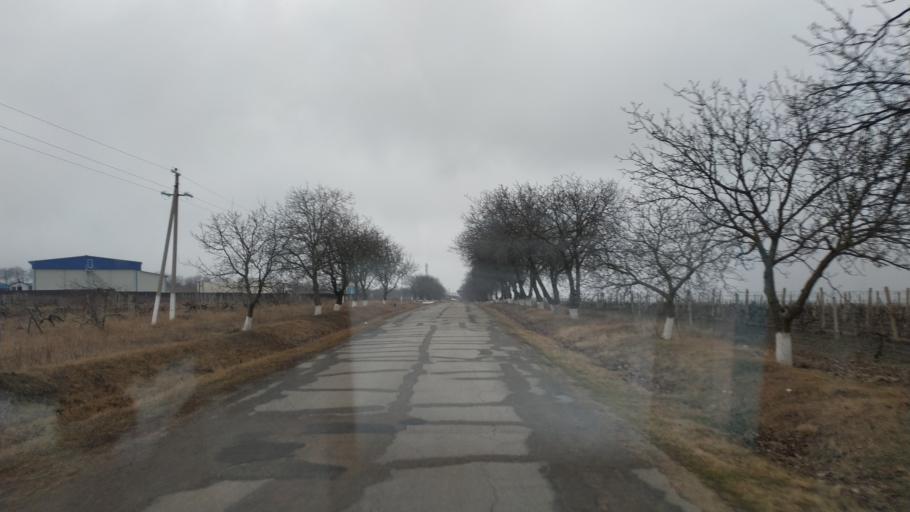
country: MD
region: Laloveni
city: Ialoveni
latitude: 46.8941
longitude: 28.6833
